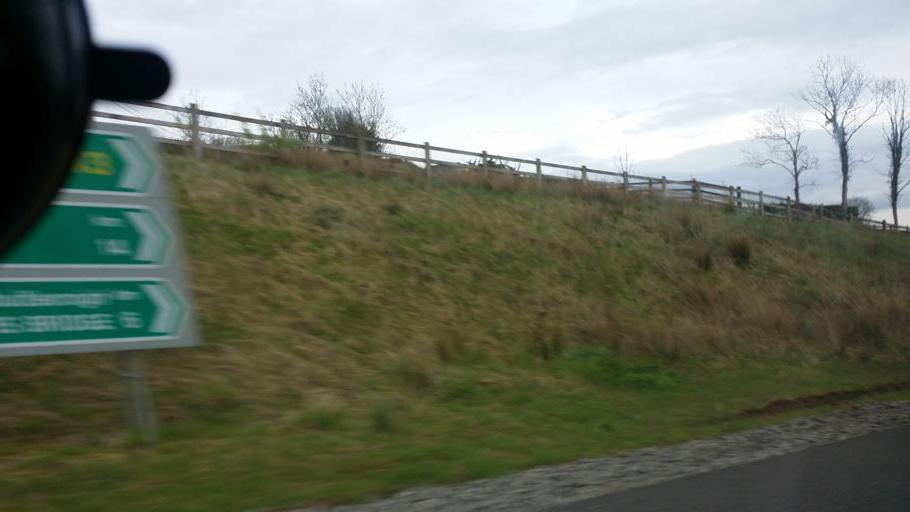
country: IE
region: Ulster
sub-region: An Cabhan
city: Belturbet
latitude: 54.0819
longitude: -7.4342
